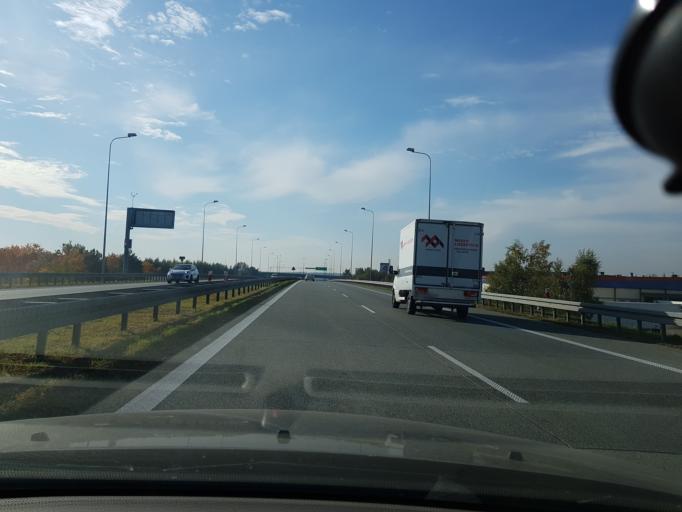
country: PL
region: Lodz Voivodeship
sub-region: Powiat rawski
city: Rawa Mazowiecka
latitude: 51.7770
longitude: 20.2755
